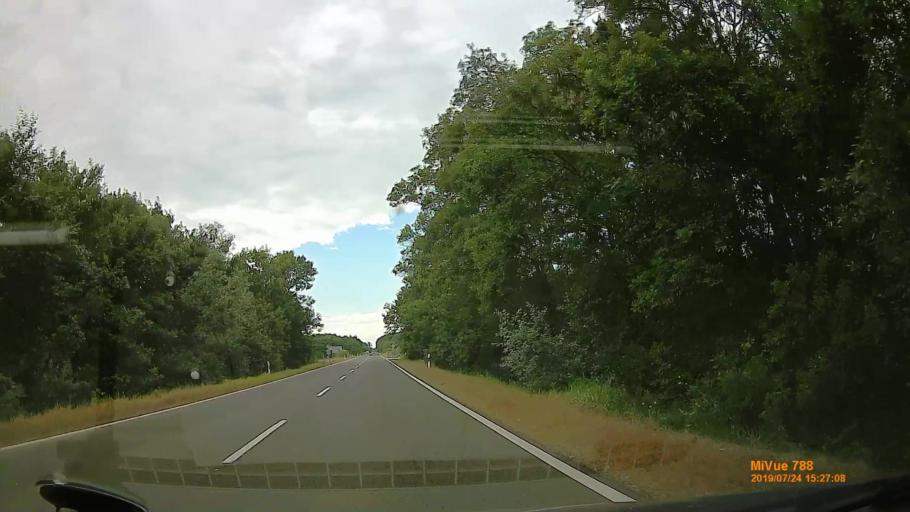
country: HU
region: Szabolcs-Szatmar-Bereg
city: Tarpa
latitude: 48.1604
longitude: 22.5081
